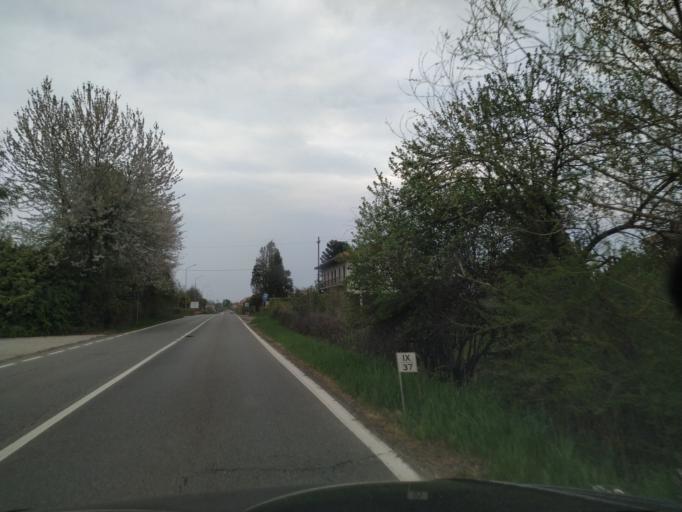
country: IT
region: Piedmont
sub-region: Provincia di Novara
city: Cureggio
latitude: 45.6626
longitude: 8.4385
